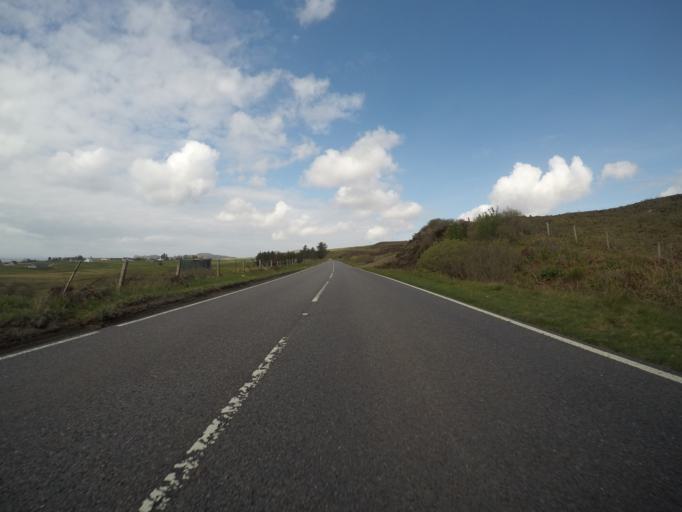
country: GB
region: Scotland
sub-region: Highland
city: Portree
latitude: 57.5570
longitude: -6.3639
